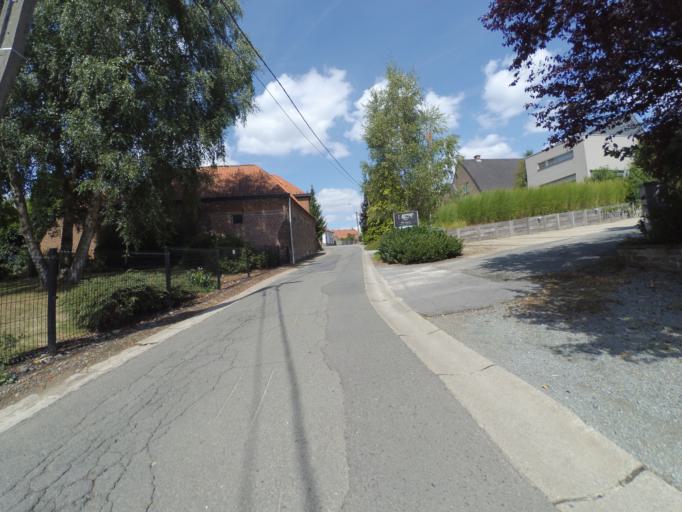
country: BE
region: Flanders
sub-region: Provincie Oost-Vlaanderen
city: Zottegem
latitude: 50.8604
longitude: 3.7970
